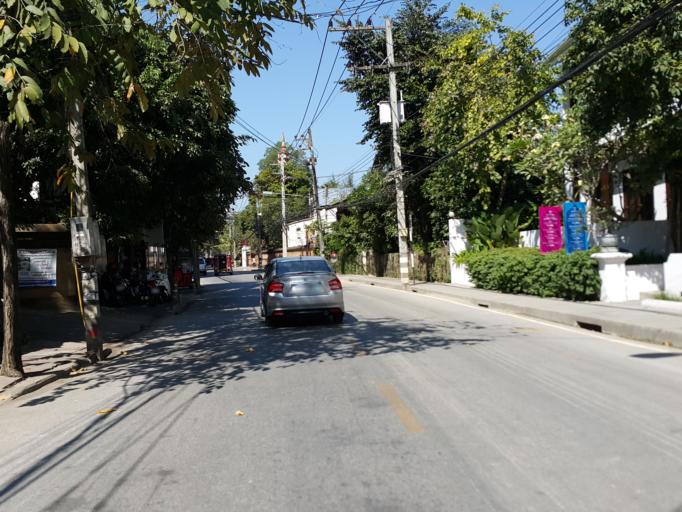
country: TH
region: Chiang Mai
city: Chiang Mai
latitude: 18.7796
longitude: 99.0045
